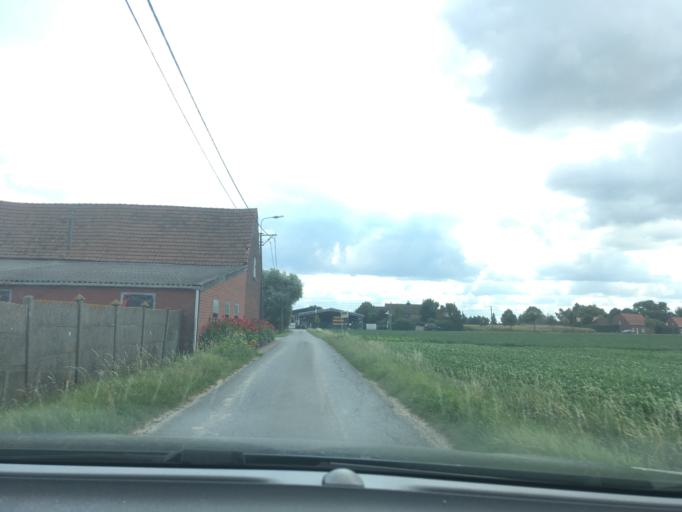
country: BE
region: Flanders
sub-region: Provincie West-Vlaanderen
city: Staden
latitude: 50.9534
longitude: 3.0423
